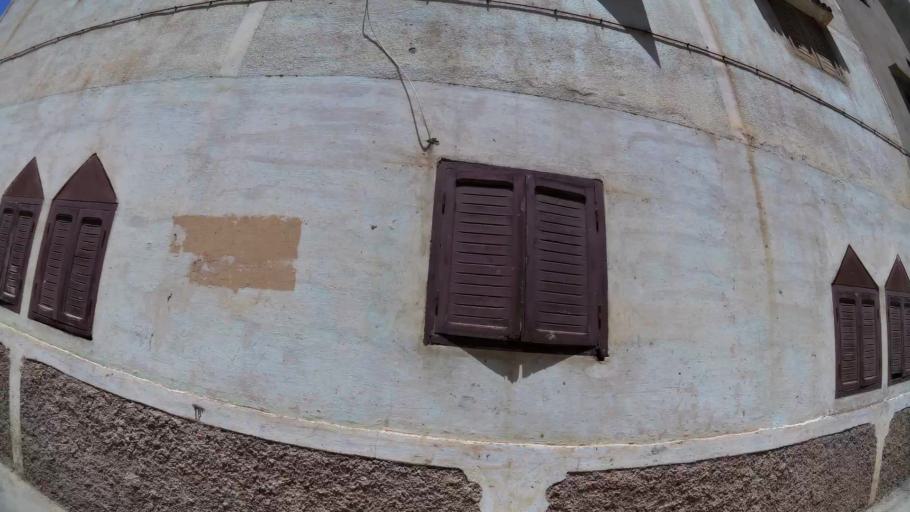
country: MA
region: Rabat-Sale-Zemmour-Zaer
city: Sale
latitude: 34.0713
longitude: -6.7844
